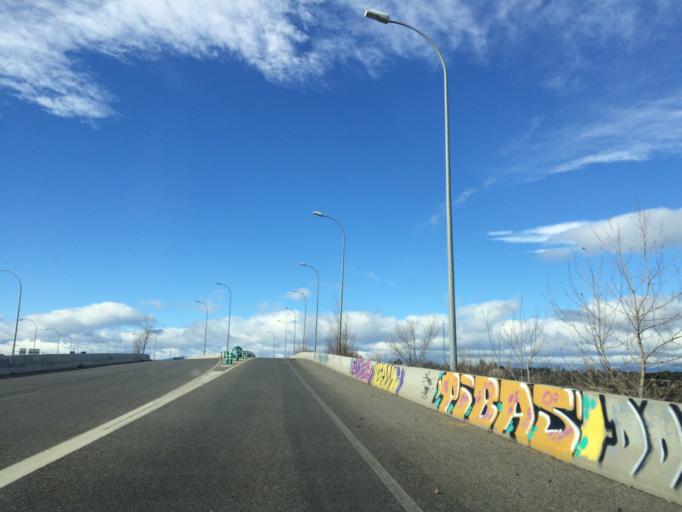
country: ES
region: Madrid
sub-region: Provincia de Madrid
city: Las Tablas
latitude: 40.5190
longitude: -3.6760
